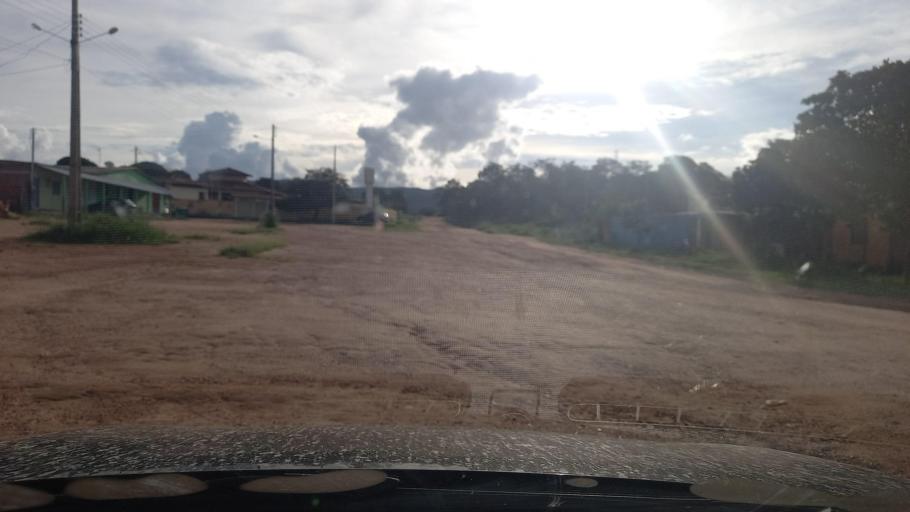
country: BR
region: Goias
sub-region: Cavalcante
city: Cavalcante
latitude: -13.7996
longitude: -47.4456
